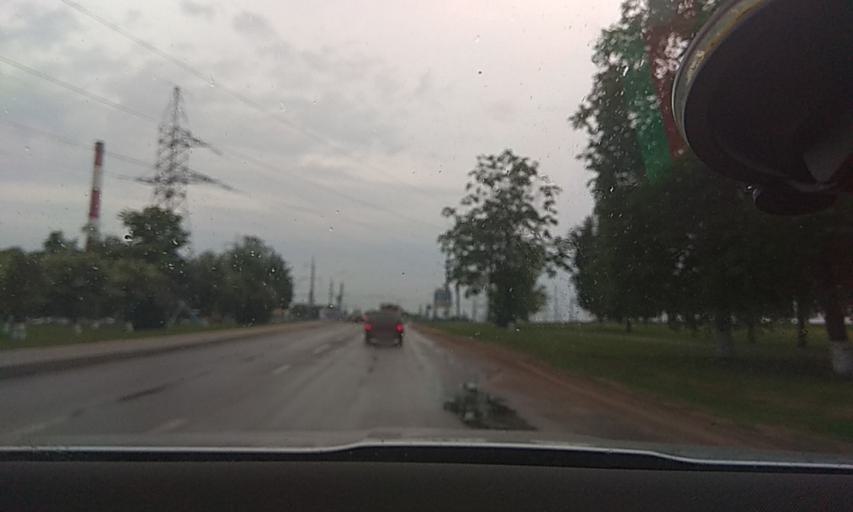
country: BY
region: Grodnenskaya
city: Hrodna
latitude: 53.6740
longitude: 23.8897
